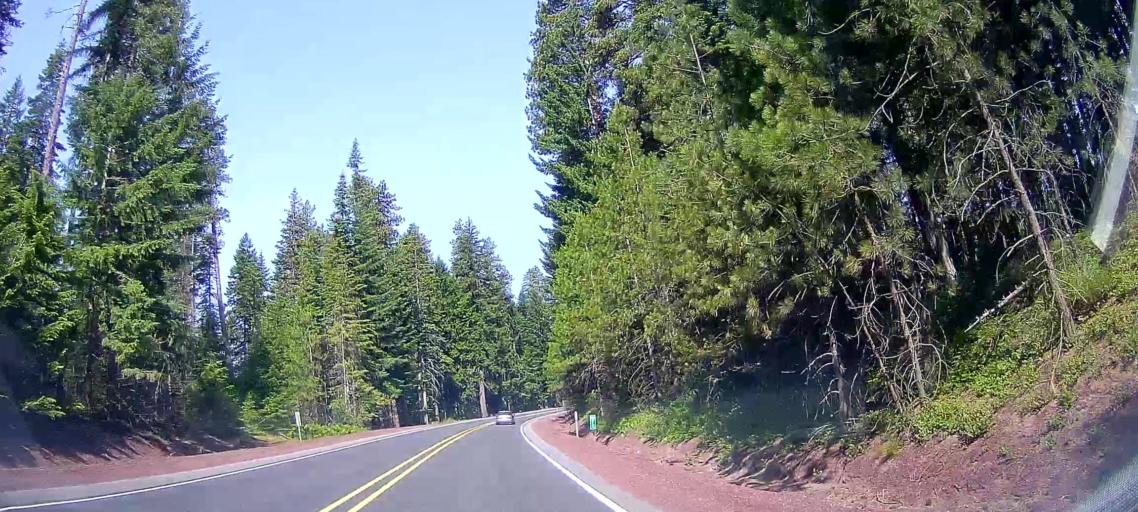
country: US
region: Oregon
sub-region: Clackamas County
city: Mount Hood Village
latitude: 45.1264
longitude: -121.5922
